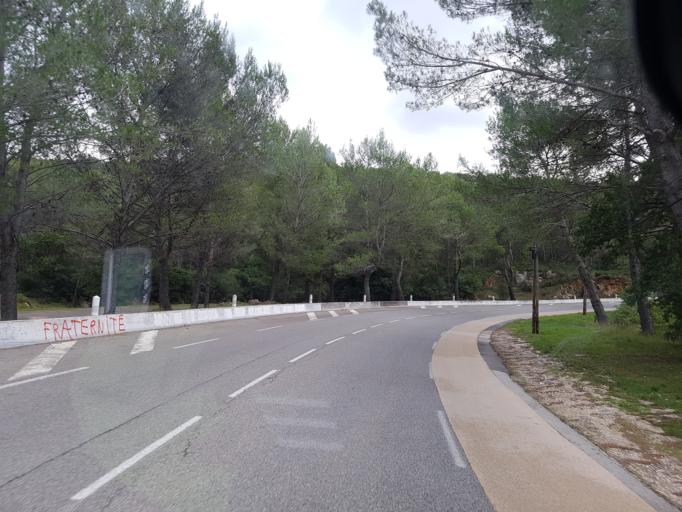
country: FR
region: Provence-Alpes-Cote d'Azur
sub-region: Departement des Bouches-du-Rhone
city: Cuges-les-Pins
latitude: 43.2747
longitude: 5.7195
